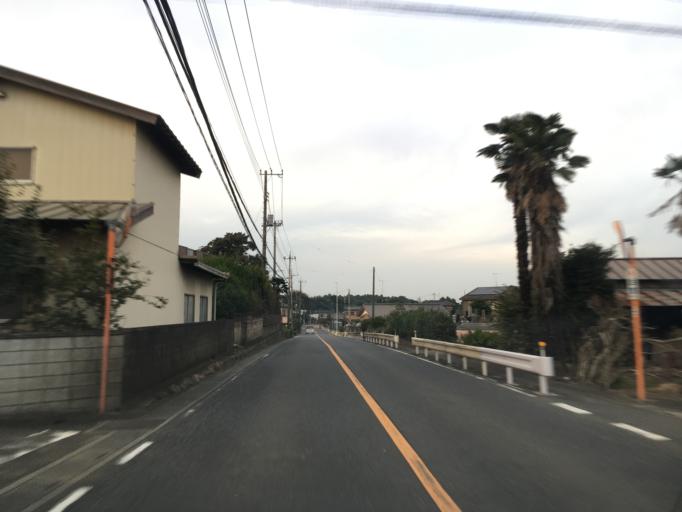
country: JP
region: Saitama
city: Sayama
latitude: 35.8762
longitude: 139.3790
